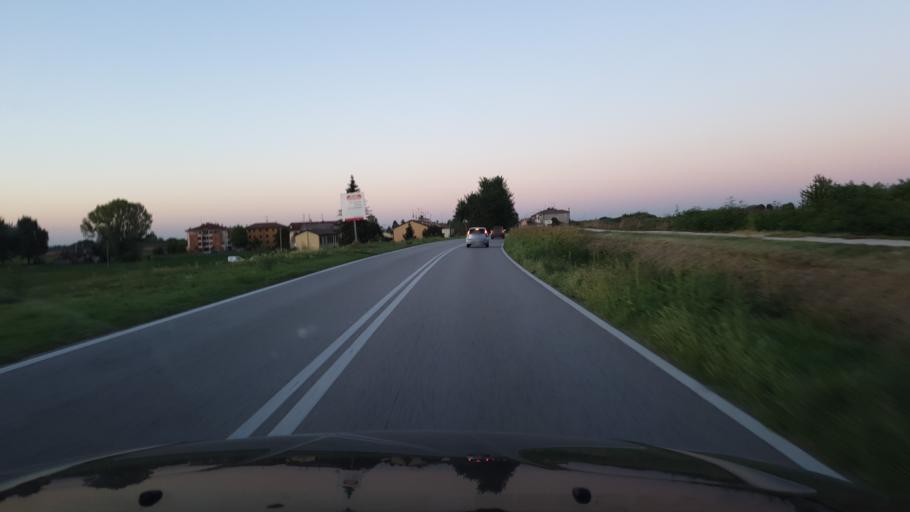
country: IT
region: Emilia-Romagna
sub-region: Provincia di Bologna
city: Ca De Fabbri
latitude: 44.6248
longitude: 11.4582
